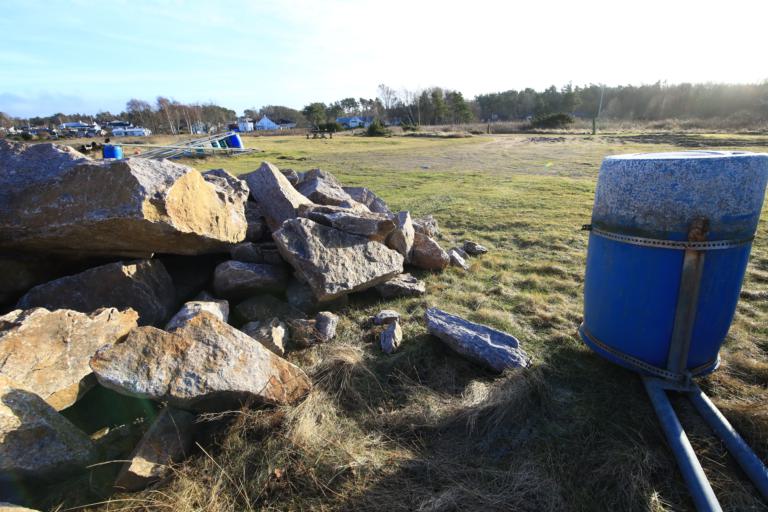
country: SE
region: Halland
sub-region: Kungsbacka Kommun
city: Frillesas
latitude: 57.1995
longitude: 12.1714
